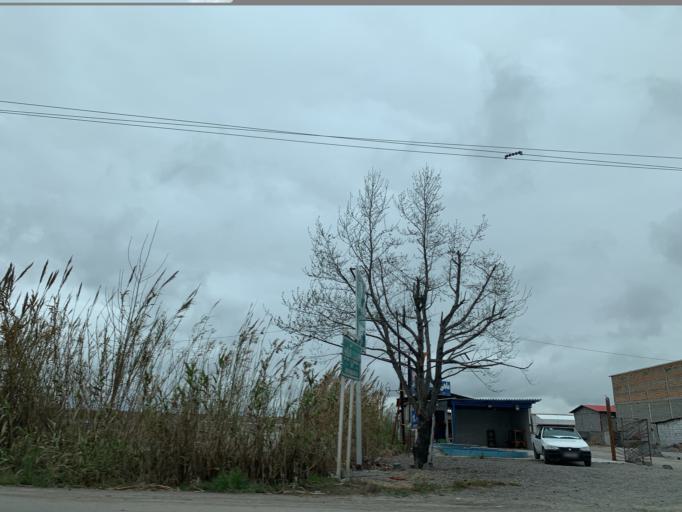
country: IR
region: Mazandaran
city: Babol
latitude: 36.5119
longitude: 52.5571
